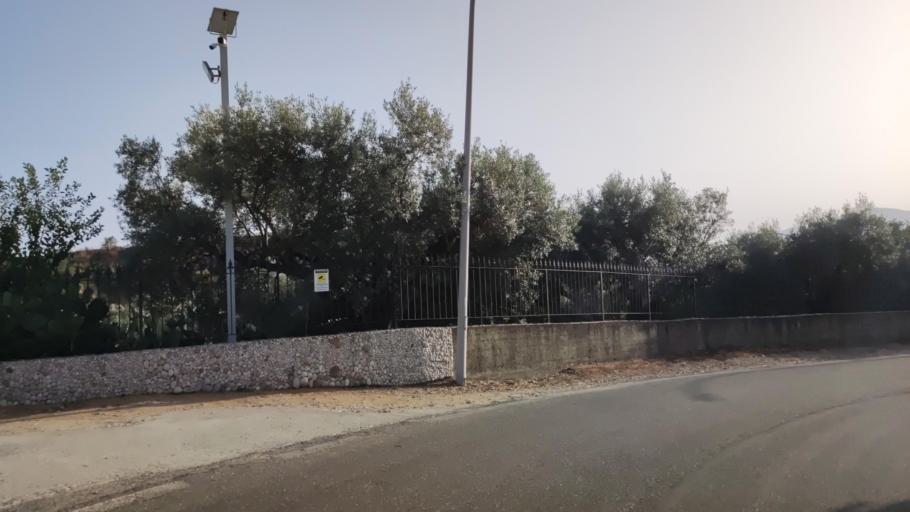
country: IT
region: Calabria
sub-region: Provincia di Reggio Calabria
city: Riace
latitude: 38.4180
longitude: 16.4786
